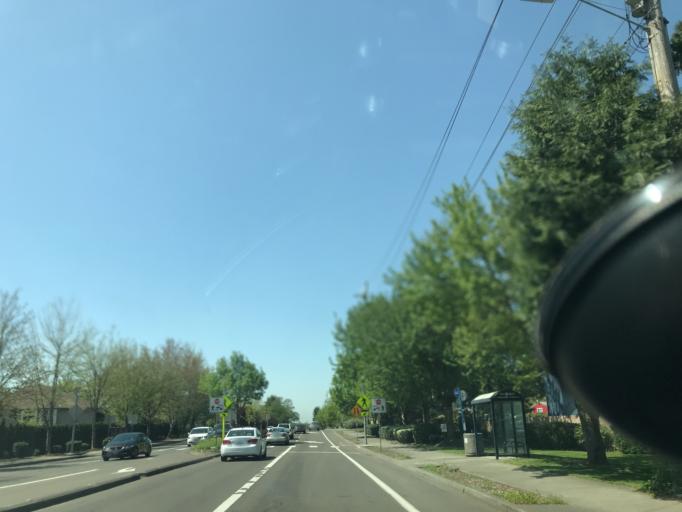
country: US
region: Oregon
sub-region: Multnomah County
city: Gresham
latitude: 45.4912
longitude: -122.4791
